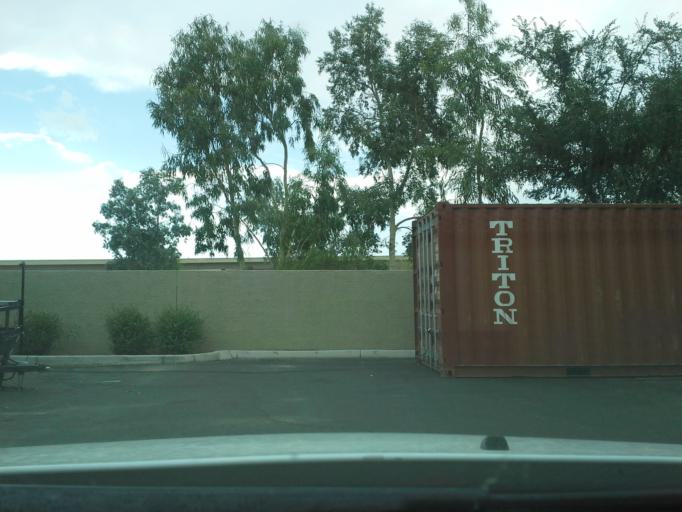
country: US
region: Arizona
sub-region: Maricopa County
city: Glendale
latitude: 33.6666
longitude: -112.1122
